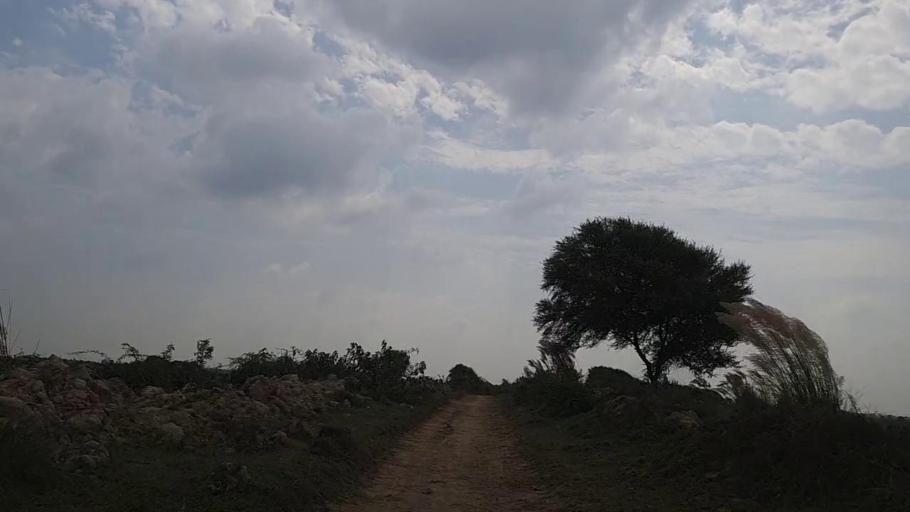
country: PK
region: Sindh
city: Mirpur Batoro
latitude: 24.6183
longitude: 68.1359
